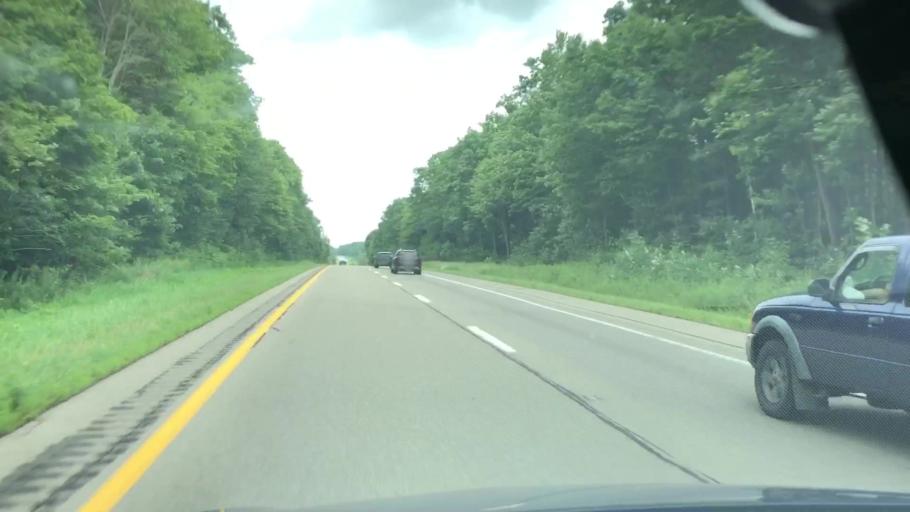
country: US
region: Pennsylvania
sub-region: Erie County
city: Edinboro
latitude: 41.8137
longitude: -80.1755
